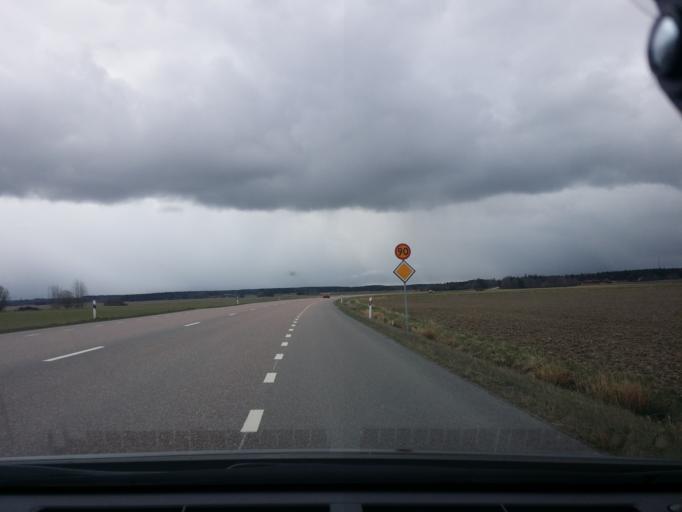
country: SE
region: Uppsala
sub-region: Enkopings Kommun
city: Irsta
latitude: 59.7522
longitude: 16.9416
